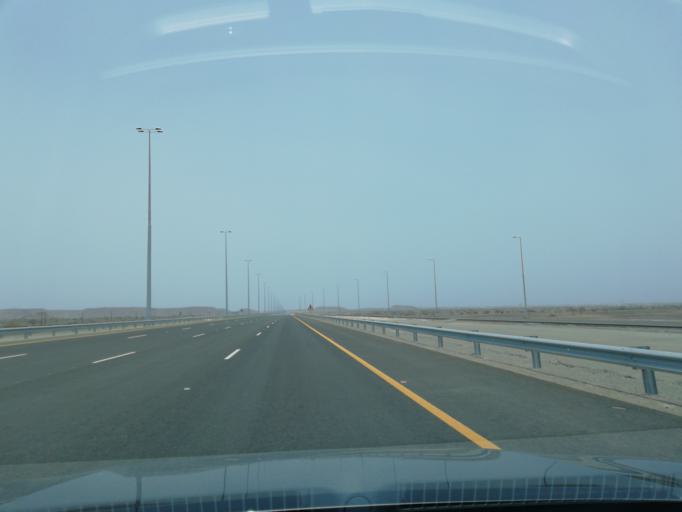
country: OM
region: Al Batinah
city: Al Liwa'
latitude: 24.4868
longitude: 56.5070
